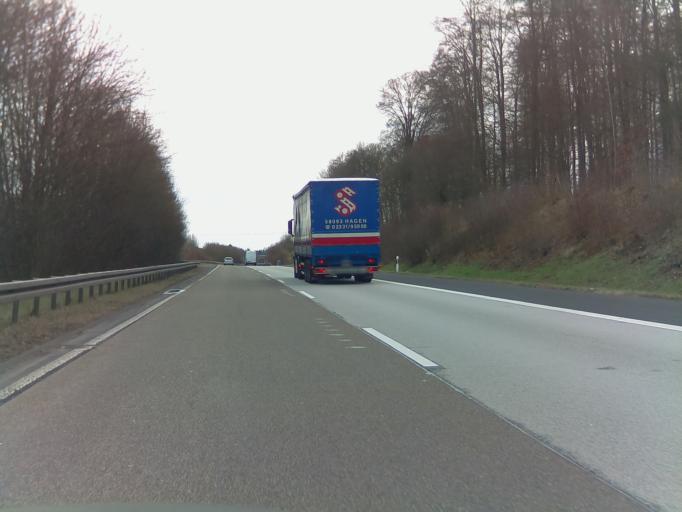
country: DE
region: Hesse
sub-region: Regierungsbezirk Darmstadt
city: Echzell
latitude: 50.3764
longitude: 8.9367
